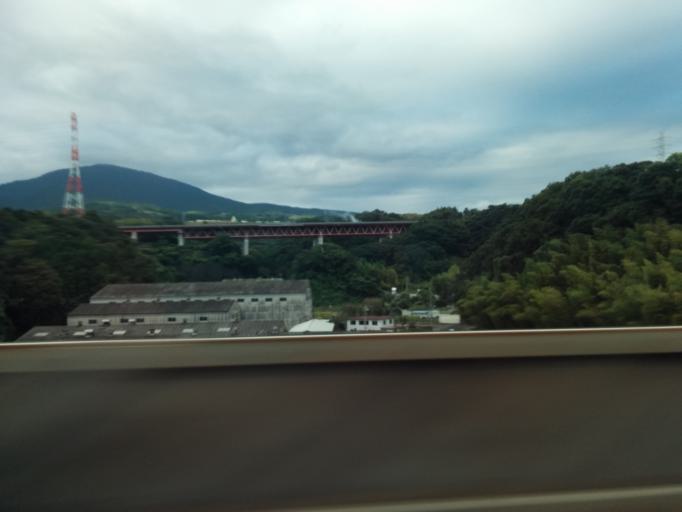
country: JP
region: Shizuoka
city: Numazu
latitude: 35.1441
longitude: 138.8027
